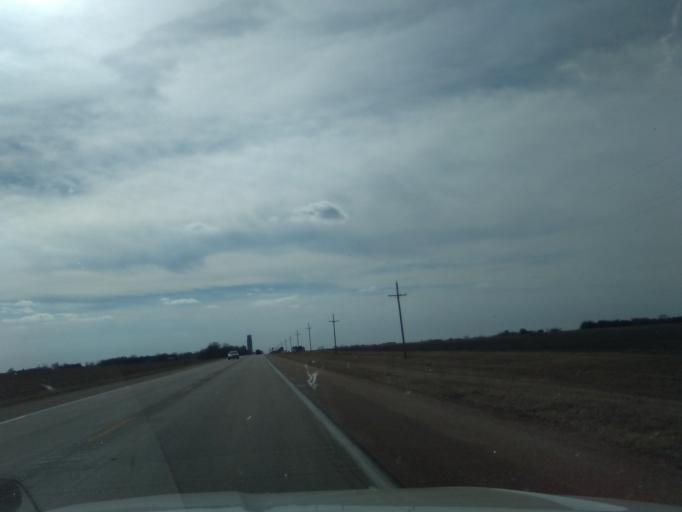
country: US
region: Nebraska
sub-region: Gage County
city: Beatrice
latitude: 40.1998
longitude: -96.9583
